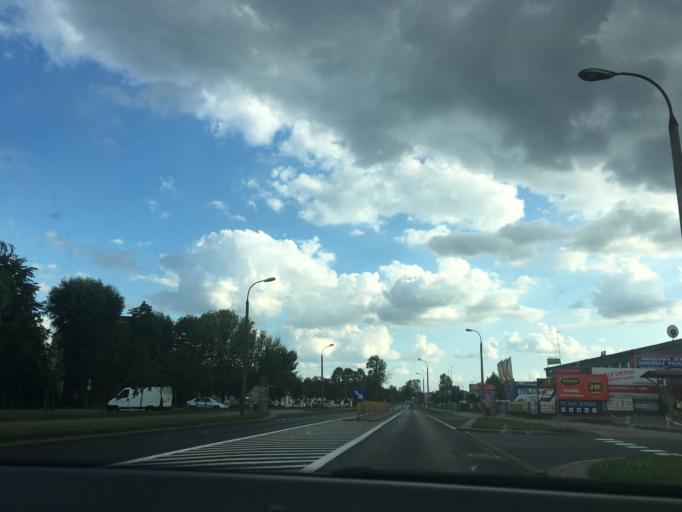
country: PL
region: Podlasie
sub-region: Powiat bielski
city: Bielsk Podlaski
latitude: 52.7753
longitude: 23.1857
